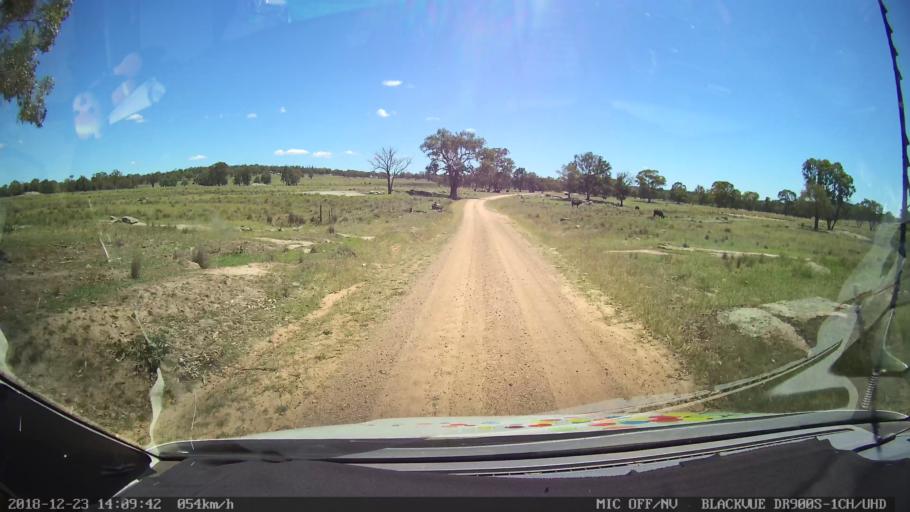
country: AU
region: New South Wales
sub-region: Tamworth Municipality
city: Manilla
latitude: -30.6467
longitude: 151.0604
